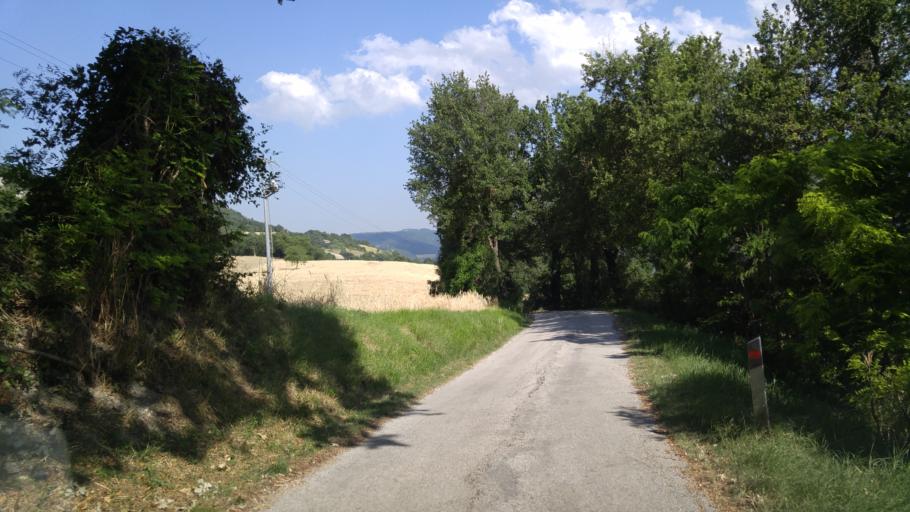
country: IT
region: The Marches
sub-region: Provincia di Pesaro e Urbino
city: Canavaccio
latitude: 43.6876
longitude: 12.7297
